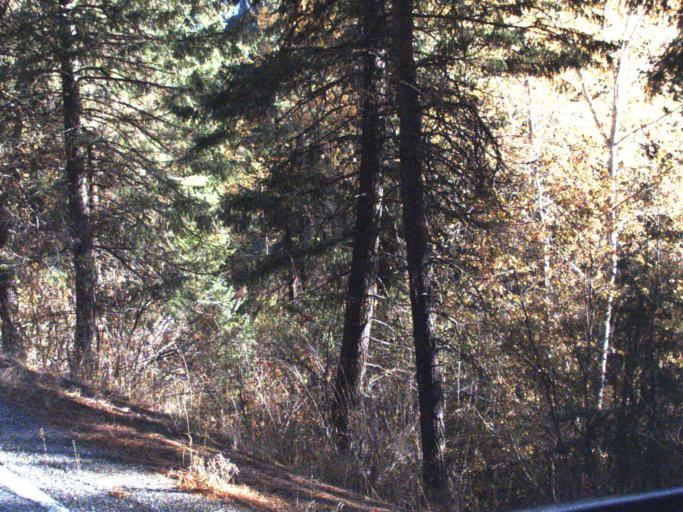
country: US
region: Washington
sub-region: Ferry County
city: Republic
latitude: 48.3732
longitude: -118.7497
